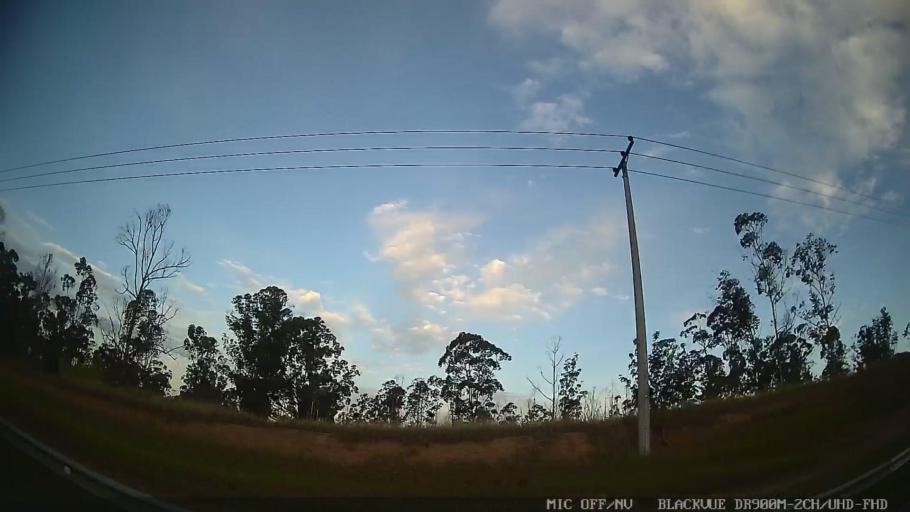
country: BR
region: Sao Paulo
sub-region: Salto
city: Salto
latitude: -23.1583
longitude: -47.2610
